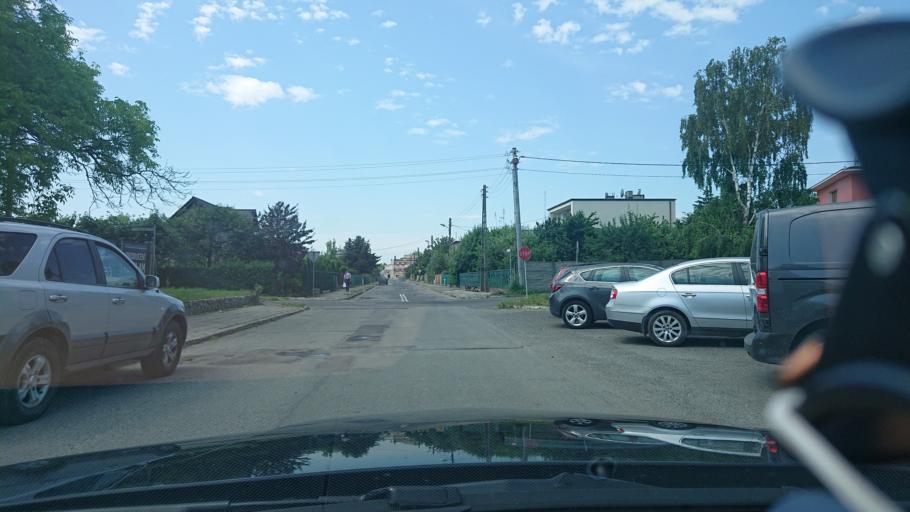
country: PL
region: Greater Poland Voivodeship
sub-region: Powiat gnieznienski
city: Gniezno
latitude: 52.5259
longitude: 17.6042
